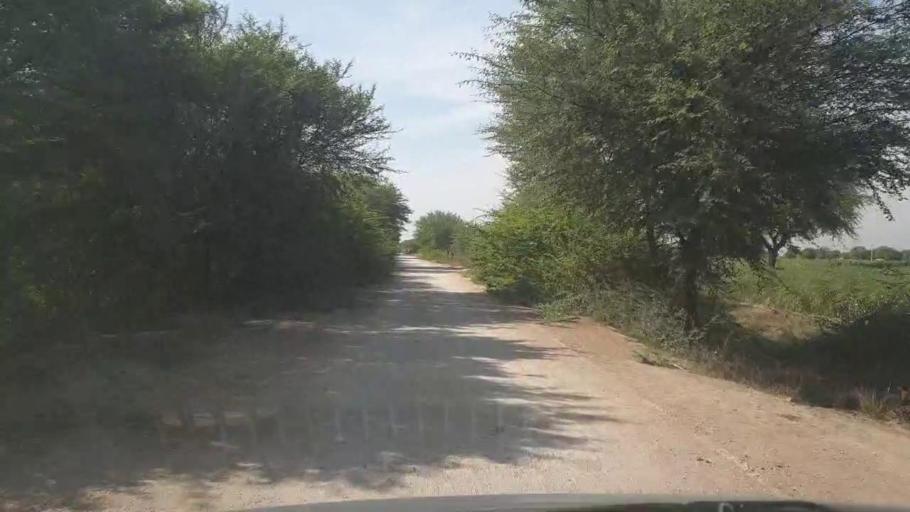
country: PK
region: Sindh
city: Kunri
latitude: 25.1822
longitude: 69.6746
